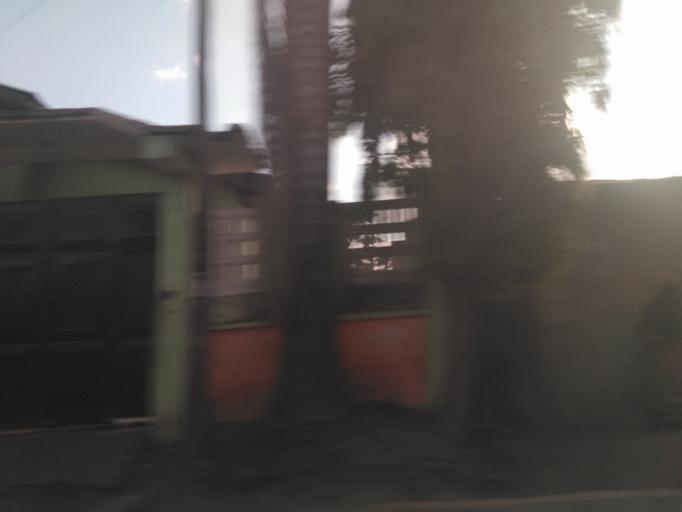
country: TZ
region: Dar es Salaam
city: Dar es Salaam
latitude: -6.8629
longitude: 39.2593
